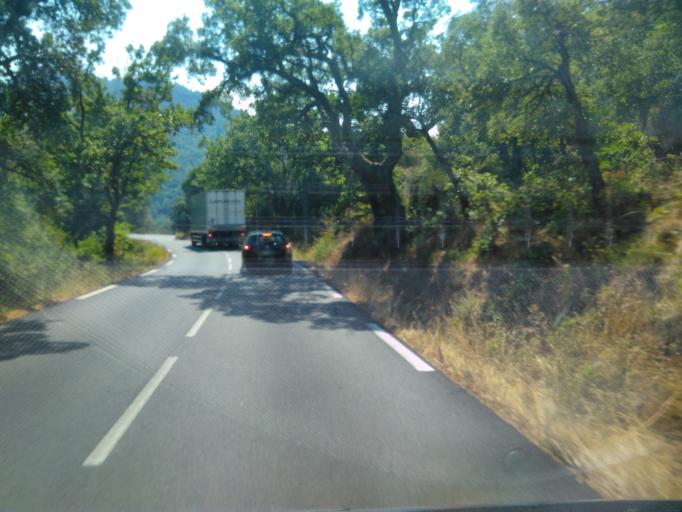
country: FR
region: Provence-Alpes-Cote d'Azur
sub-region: Departement du Var
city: La Garde-Freinet
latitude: 43.3286
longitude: 6.4664
